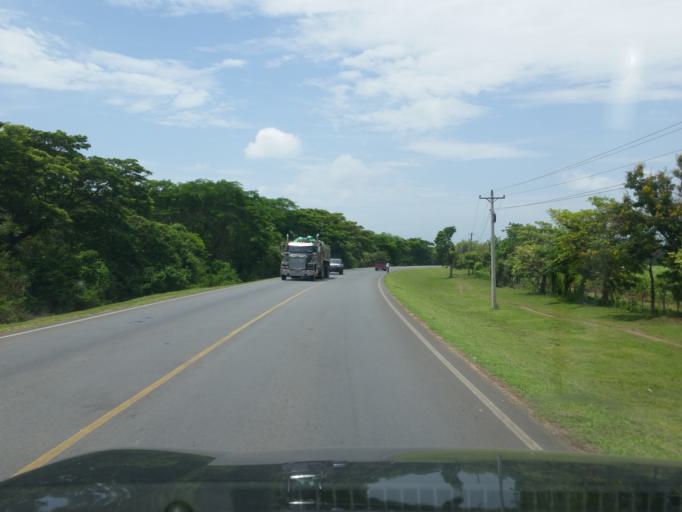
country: NI
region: Granada
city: Nandaime
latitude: 11.7476
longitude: -86.0281
